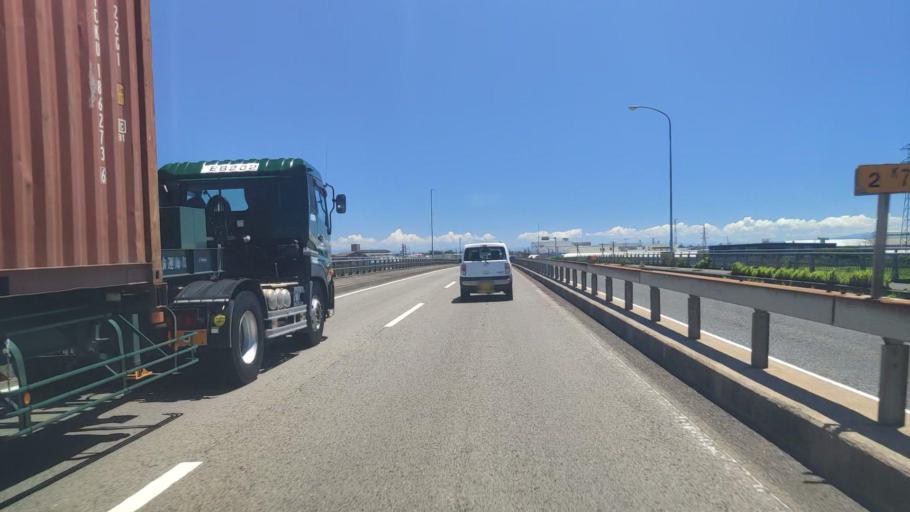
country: JP
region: Mie
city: Suzuka
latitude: 34.9075
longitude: 136.6054
